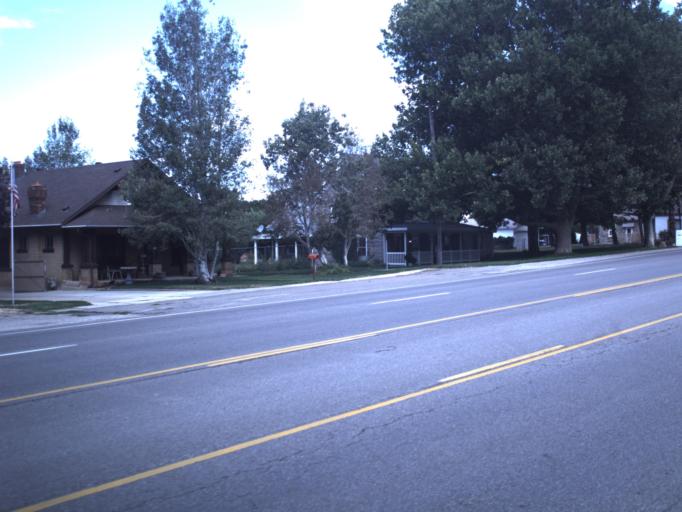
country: US
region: Utah
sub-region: Box Elder County
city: Willard
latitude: 41.4061
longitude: -112.0363
